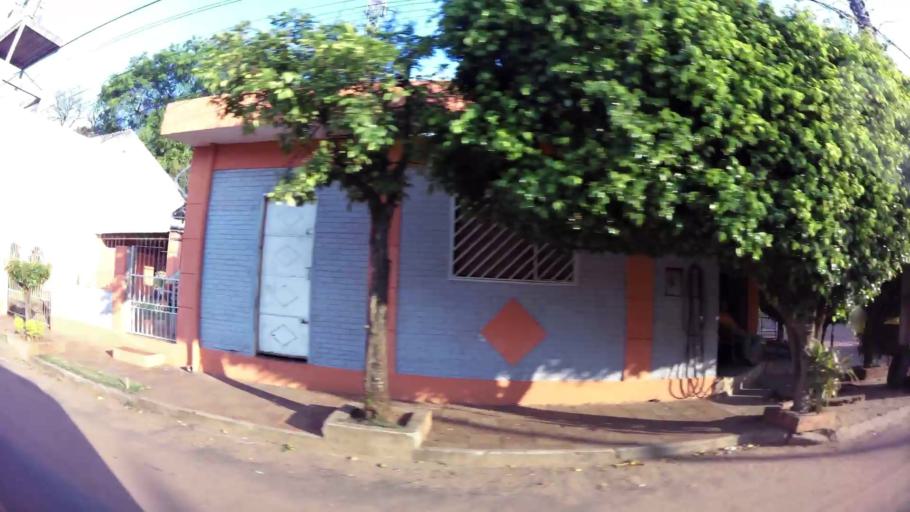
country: PY
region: Central
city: Fernando de la Mora
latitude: -25.3468
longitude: -57.5215
